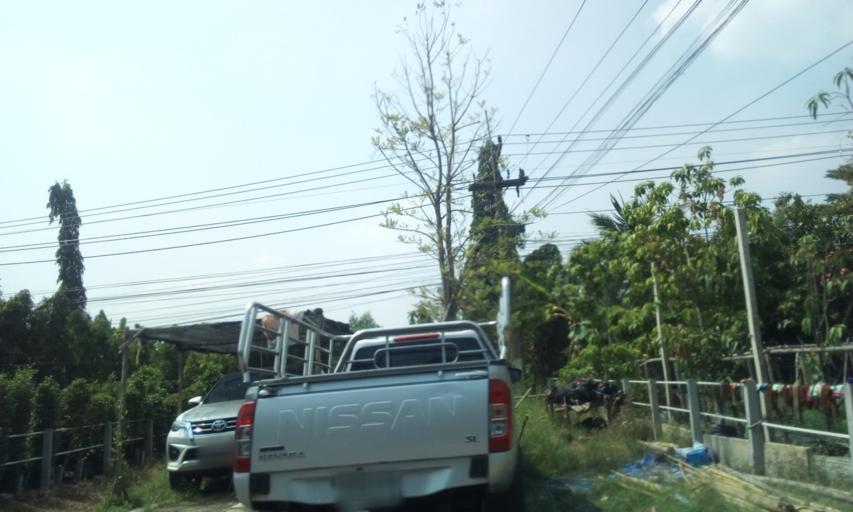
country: TH
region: Nakhon Nayok
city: Ongkharak
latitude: 14.1082
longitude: 100.9436
